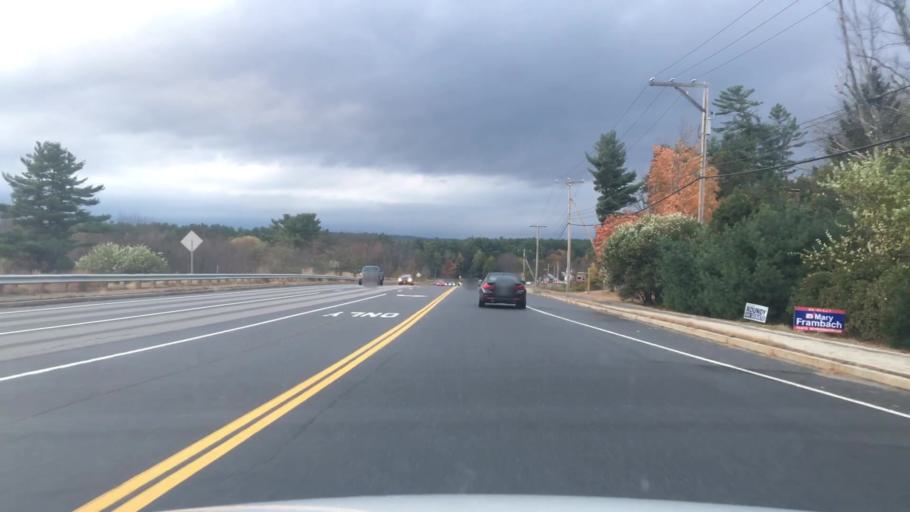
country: US
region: New Hampshire
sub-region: Merrimack County
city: Epsom
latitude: 43.2265
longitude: -71.3511
